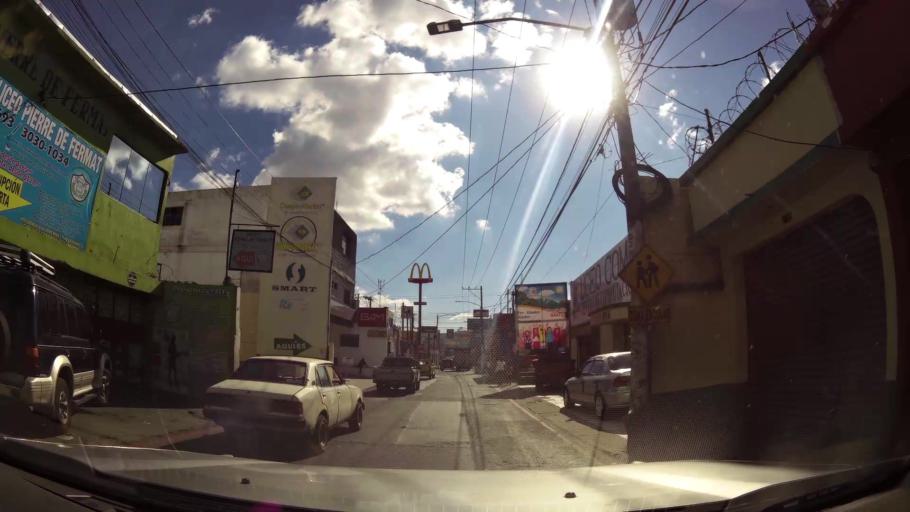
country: GT
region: Guatemala
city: Villa Nueva
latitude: 14.5274
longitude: -90.5884
